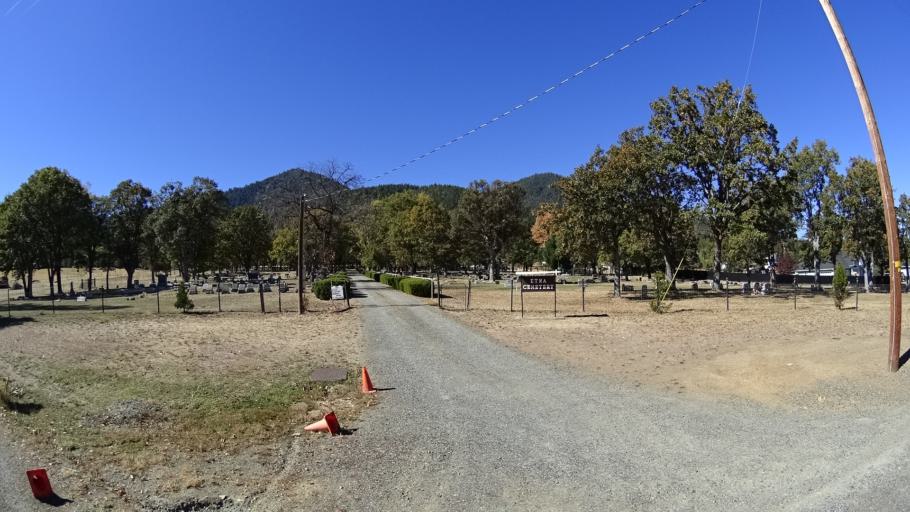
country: US
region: California
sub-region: Siskiyou County
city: Yreka
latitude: 41.4523
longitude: -122.8984
